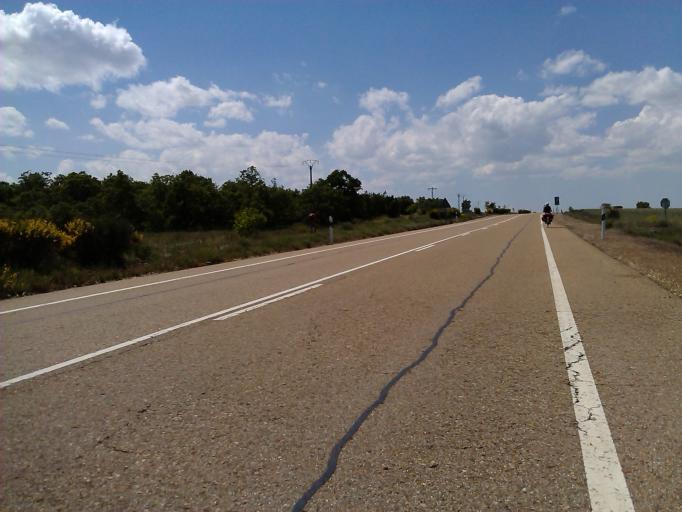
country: ES
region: Castille and Leon
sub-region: Provincia de Palencia
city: Ledigos
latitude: 42.3444
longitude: -4.8463
